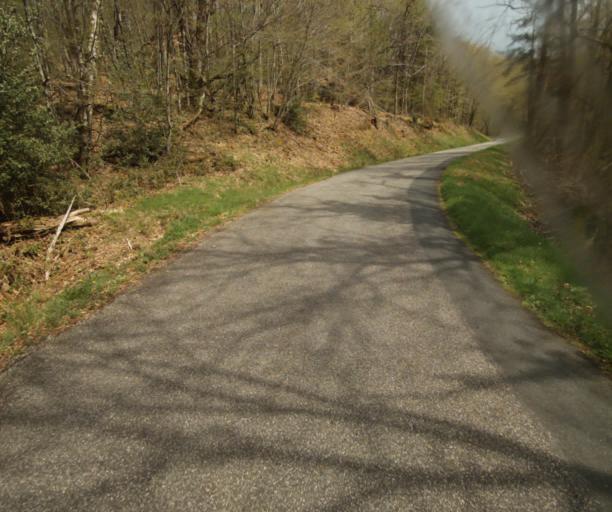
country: FR
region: Limousin
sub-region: Departement de la Correze
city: Naves
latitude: 45.3100
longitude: 1.8015
